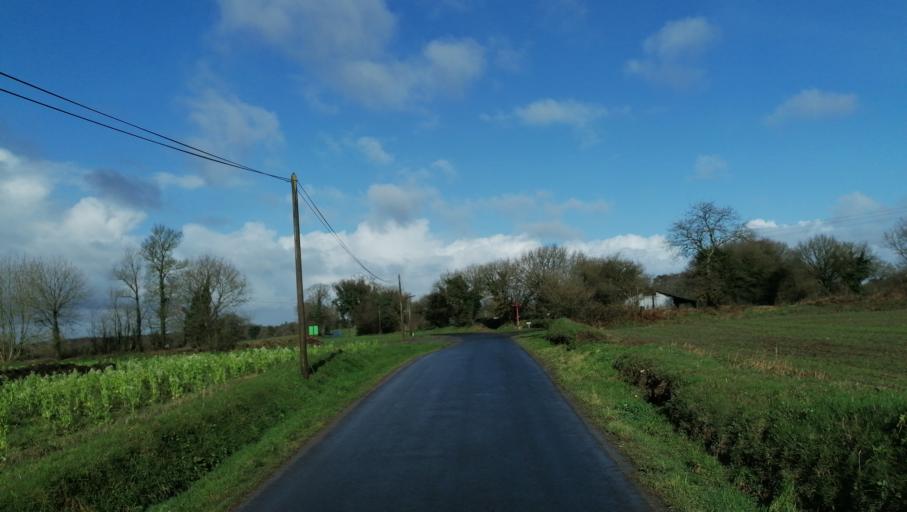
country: FR
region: Brittany
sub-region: Departement des Cotes-d'Armor
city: Lanrodec
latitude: 48.4969
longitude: -3.0155
